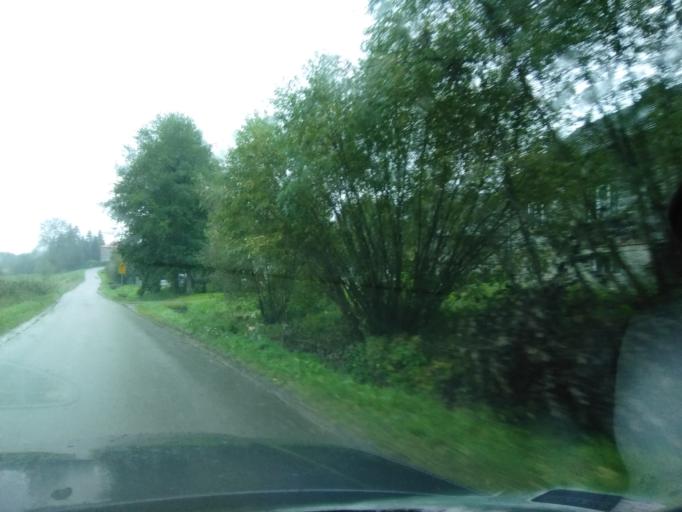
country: PL
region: Subcarpathian Voivodeship
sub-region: Powiat ropczycko-sedziszowski
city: Niedzwiada
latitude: 50.0203
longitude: 21.5415
